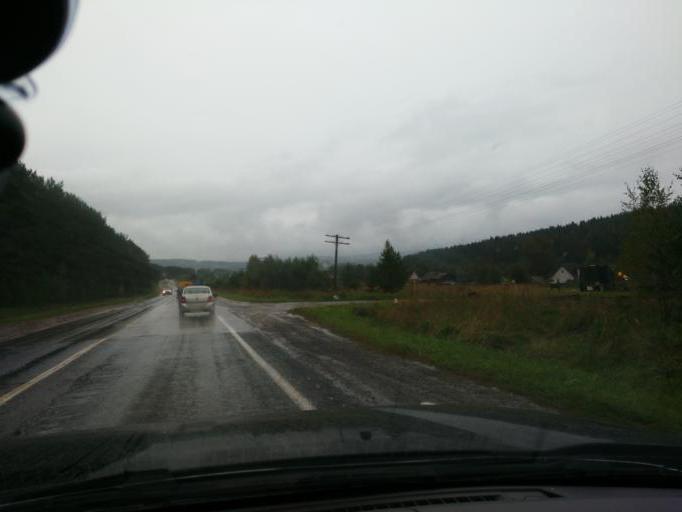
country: RU
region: Perm
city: Yugo-Kamskiy
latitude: 57.6793
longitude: 55.5761
